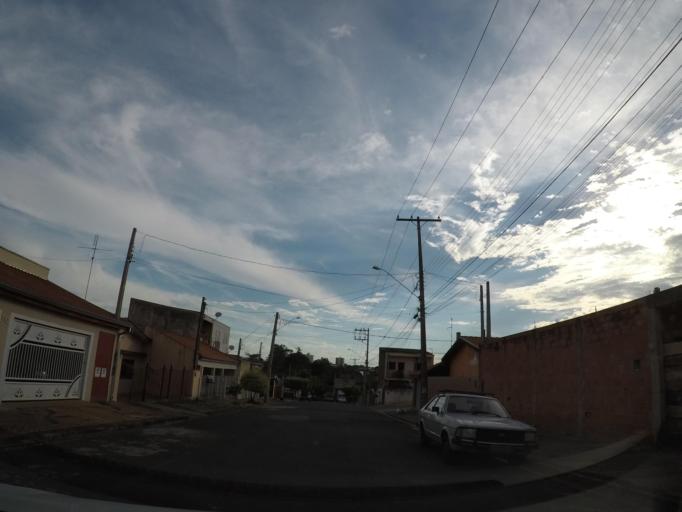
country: BR
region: Sao Paulo
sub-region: Sumare
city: Sumare
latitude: -22.8160
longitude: -47.2580
